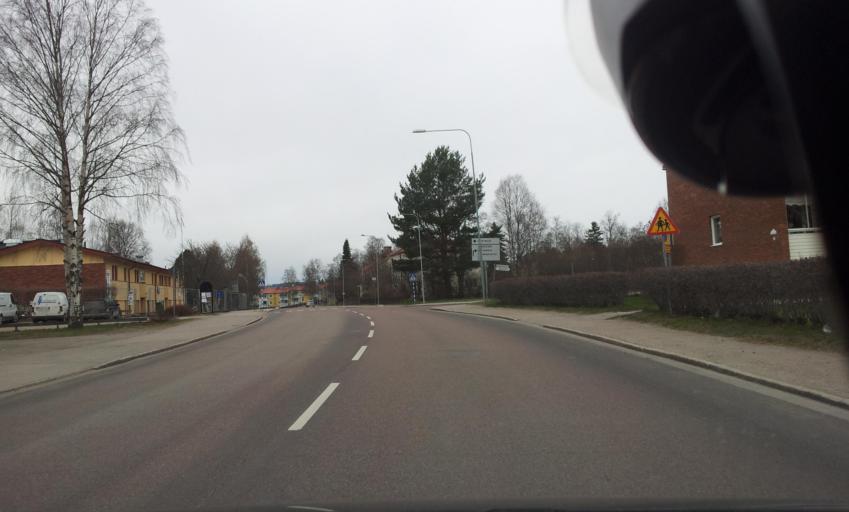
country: SE
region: Gaevleborg
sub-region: Ljusdals Kommun
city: Ljusdal
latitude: 61.8258
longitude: 16.1091
